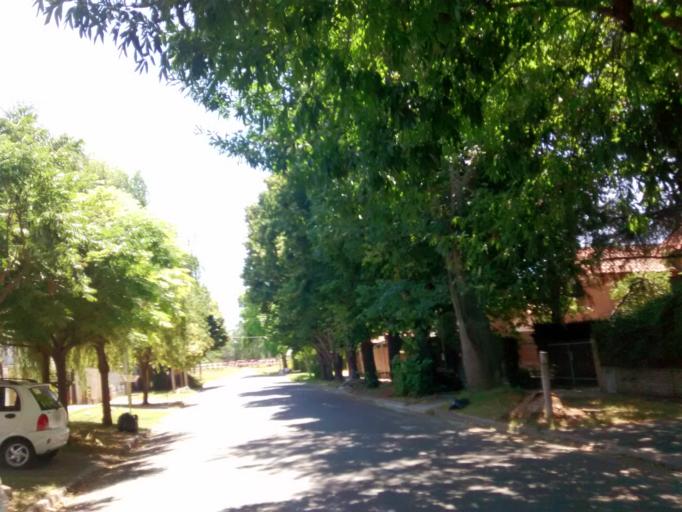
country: AR
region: Buenos Aires
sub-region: Partido de La Plata
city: La Plata
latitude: -34.8829
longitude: -58.0052
